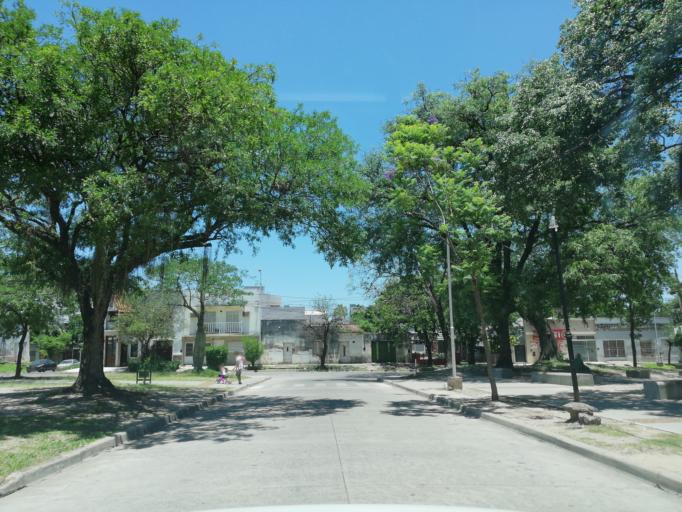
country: AR
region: Corrientes
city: Corrientes
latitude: -27.4609
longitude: -58.8274
